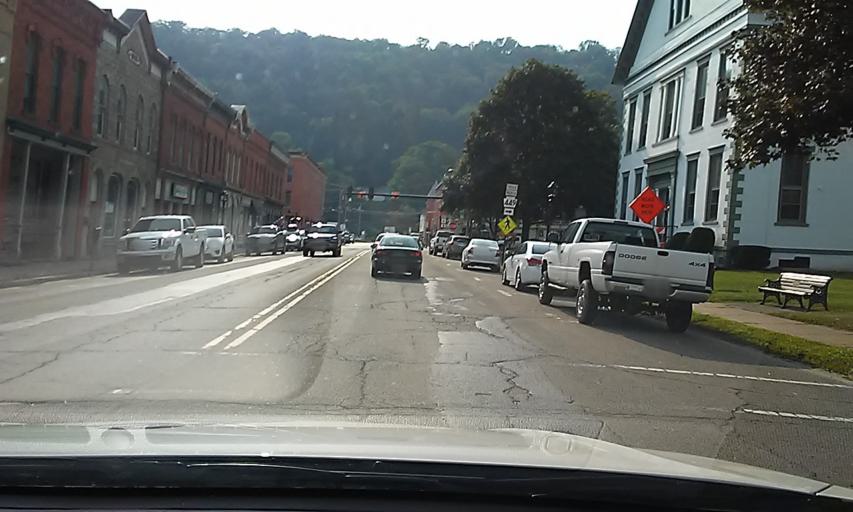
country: US
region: Pennsylvania
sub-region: Potter County
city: Coudersport
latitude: 41.7746
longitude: -78.0199
